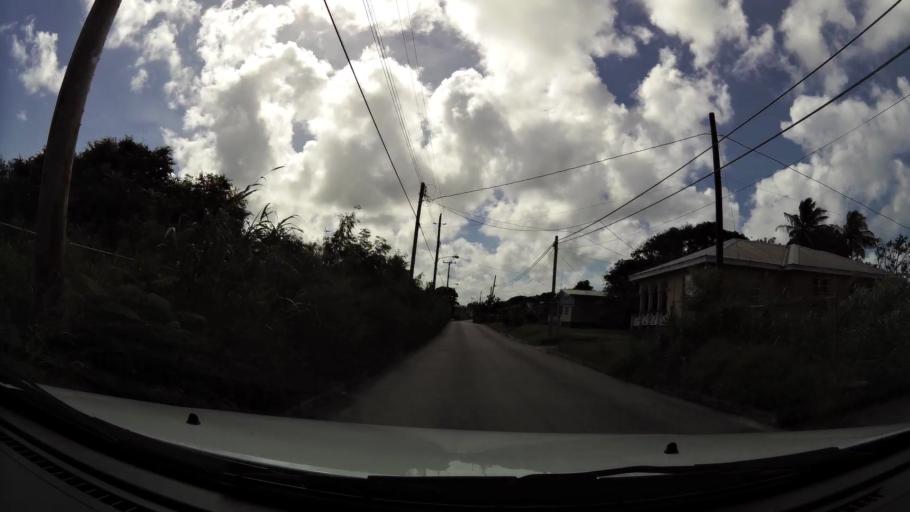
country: BB
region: Saint Lucy
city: Checker Hall
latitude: 13.2891
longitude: -59.6407
